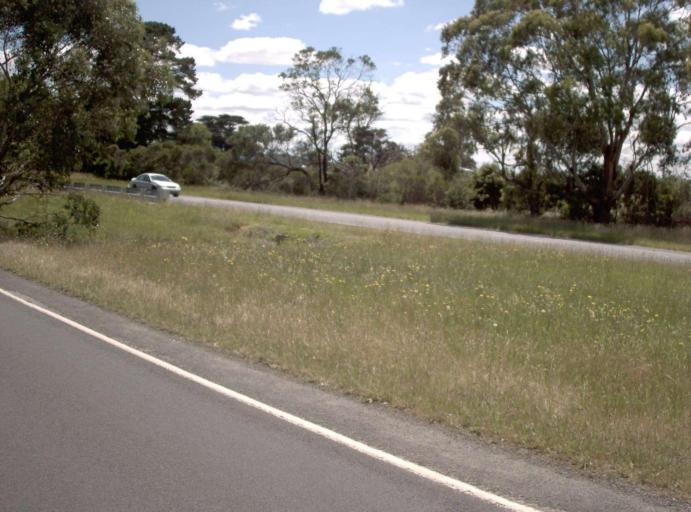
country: AU
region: Victoria
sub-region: Cardinia
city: Koo-Wee-Rup
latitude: -38.2871
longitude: 145.5462
